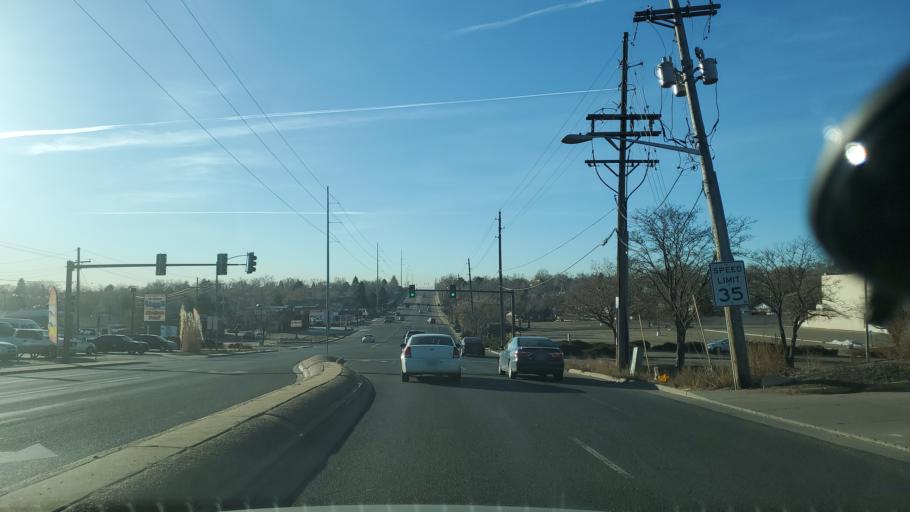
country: US
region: Colorado
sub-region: Adams County
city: Thornton
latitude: 39.8486
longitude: -104.9780
